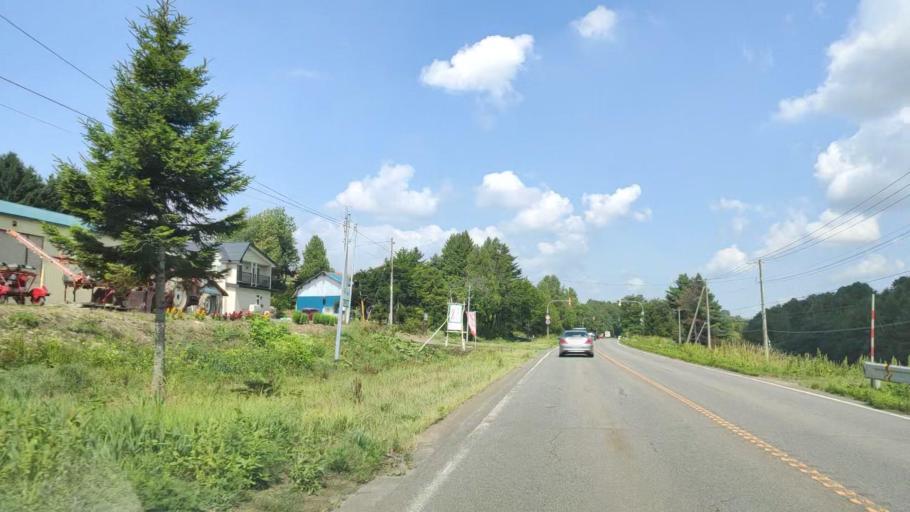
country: JP
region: Hokkaido
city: Shimo-furano
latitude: 43.5533
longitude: 142.4375
